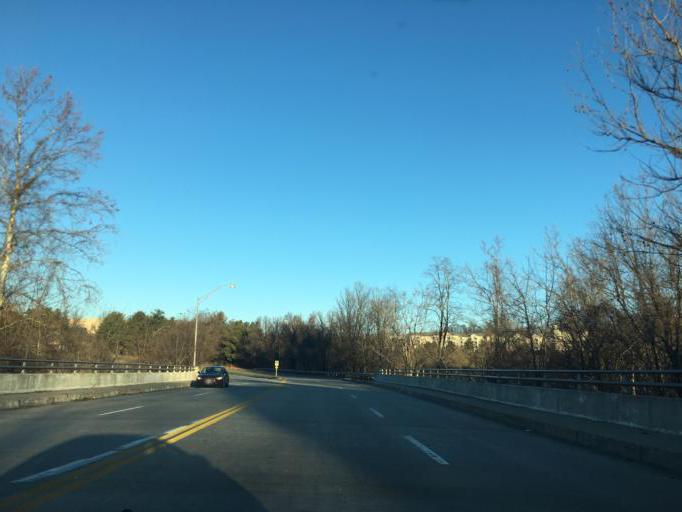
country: US
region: Maryland
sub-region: Baltimore County
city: Owings Mills
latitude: 39.4029
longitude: -76.7840
